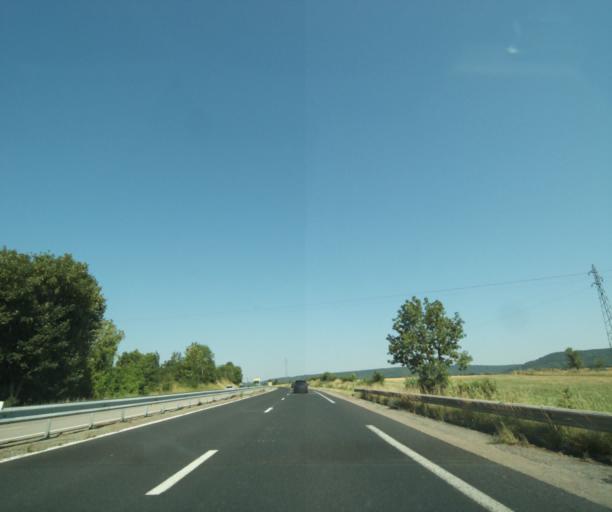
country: FR
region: Lorraine
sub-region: Departement de Meurthe-et-Moselle
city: Ecrouves
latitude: 48.6640
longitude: 5.8301
